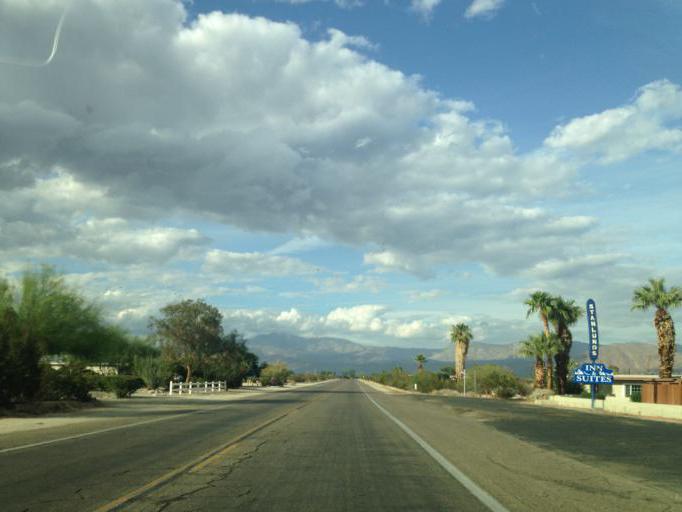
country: US
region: California
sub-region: San Diego County
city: Borrego Springs
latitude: 33.2453
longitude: -116.3744
